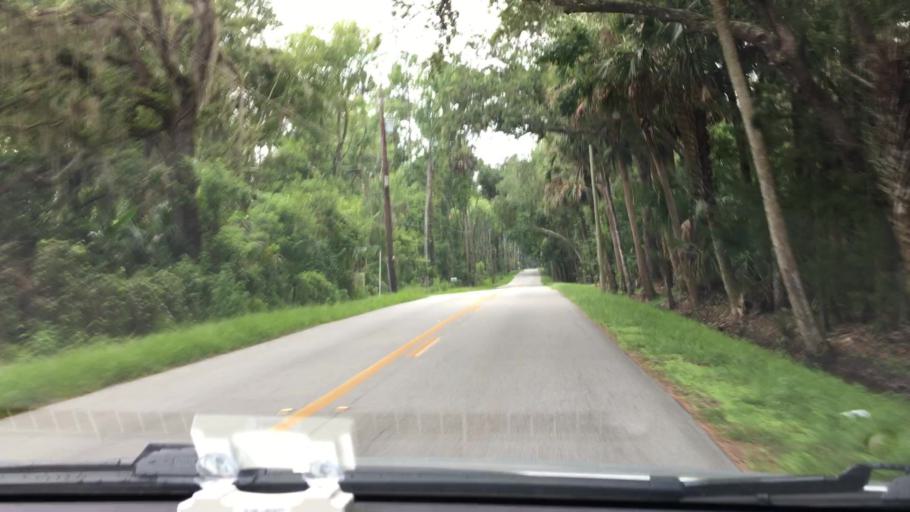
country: US
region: Florida
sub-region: Volusia County
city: Deltona
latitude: 28.8600
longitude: -81.2354
